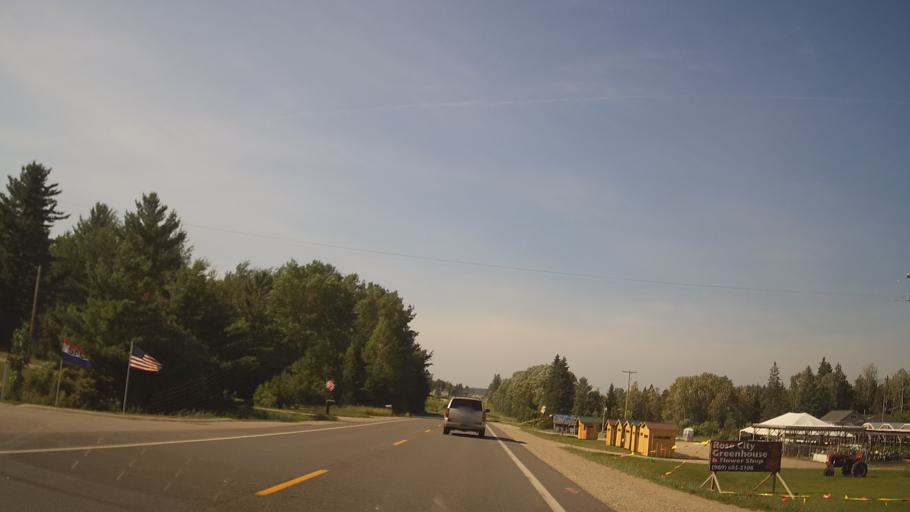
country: US
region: Michigan
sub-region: Ogemaw County
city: West Branch
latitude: 44.4014
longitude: -84.1164
